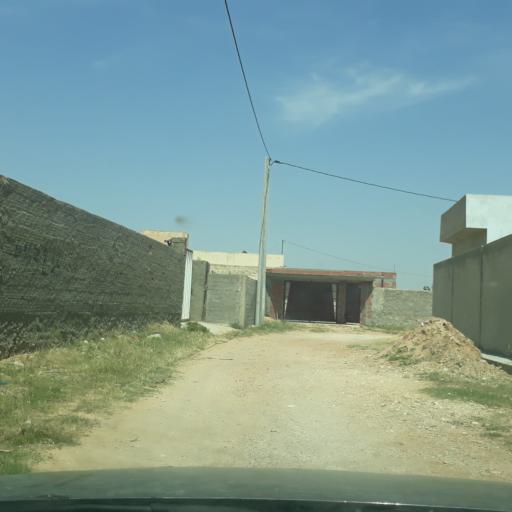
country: TN
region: Safaqis
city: Al Qarmadah
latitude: 34.8247
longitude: 10.7810
